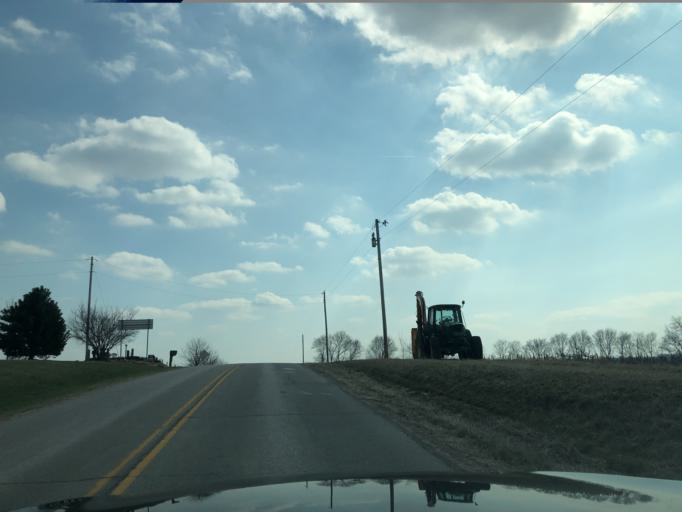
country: US
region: Missouri
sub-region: Platte County
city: Weston
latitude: 39.4968
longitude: -94.8454
